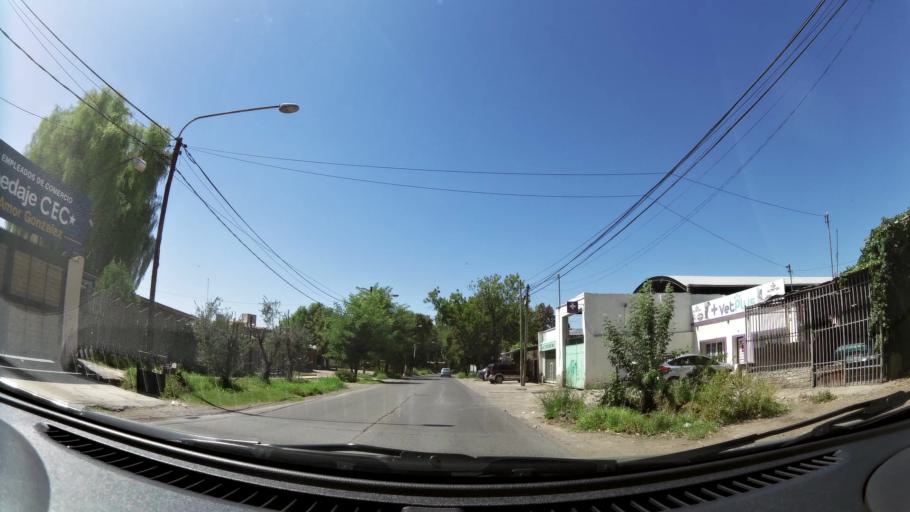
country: AR
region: Mendoza
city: Villa Nueva
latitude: -32.8680
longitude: -68.7892
